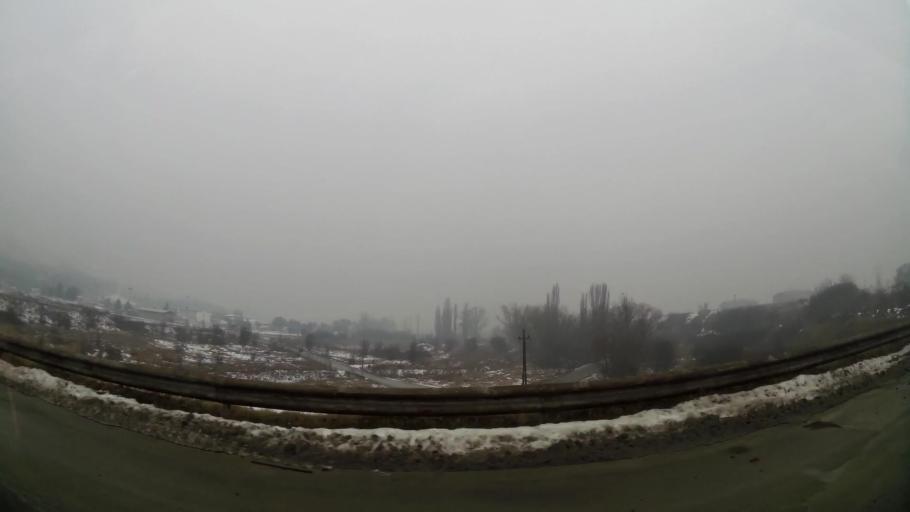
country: MK
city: Miladinovci
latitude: 41.9984
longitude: 21.6599
